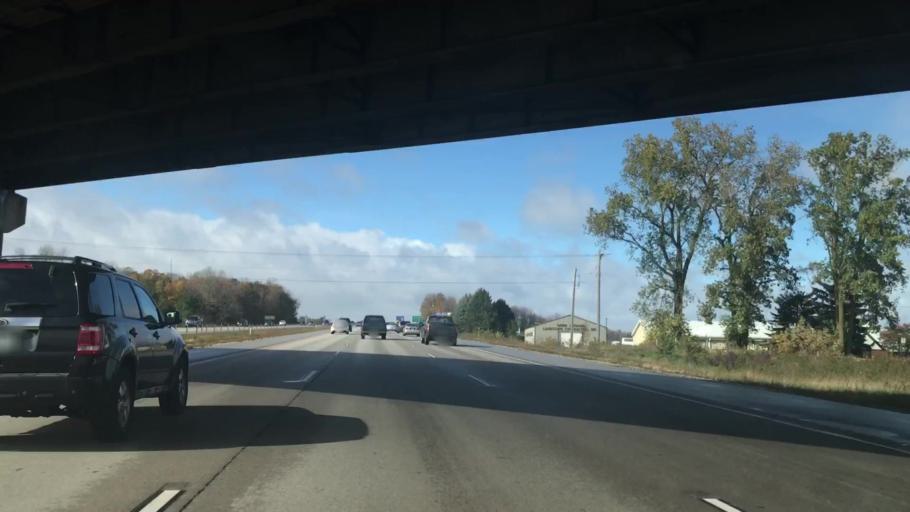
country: US
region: Wisconsin
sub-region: Washington County
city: Richfield
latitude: 43.2361
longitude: -88.1738
